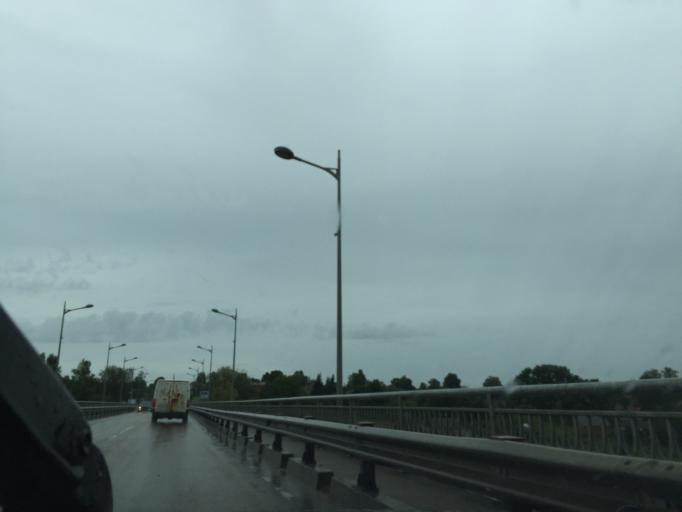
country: LV
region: Jekabpils Rajons
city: Jekabpils
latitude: 56.4995
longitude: 25.8785
